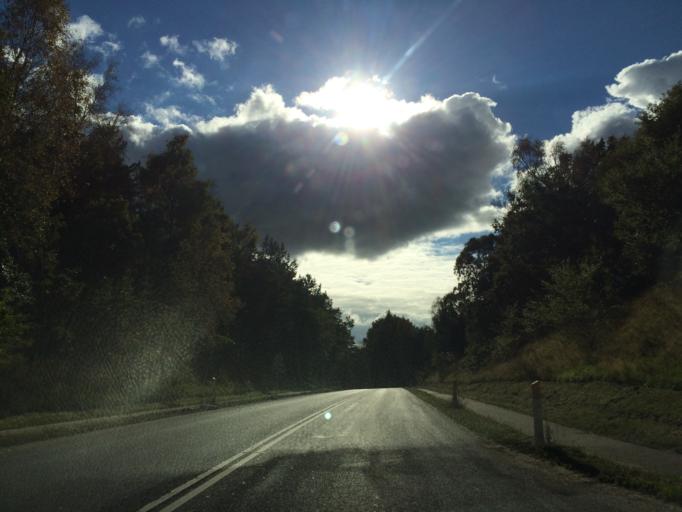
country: DK
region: Central Jutland
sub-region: Skanderborg Kommune
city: Ry
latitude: 56.1110
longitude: 9.7857
